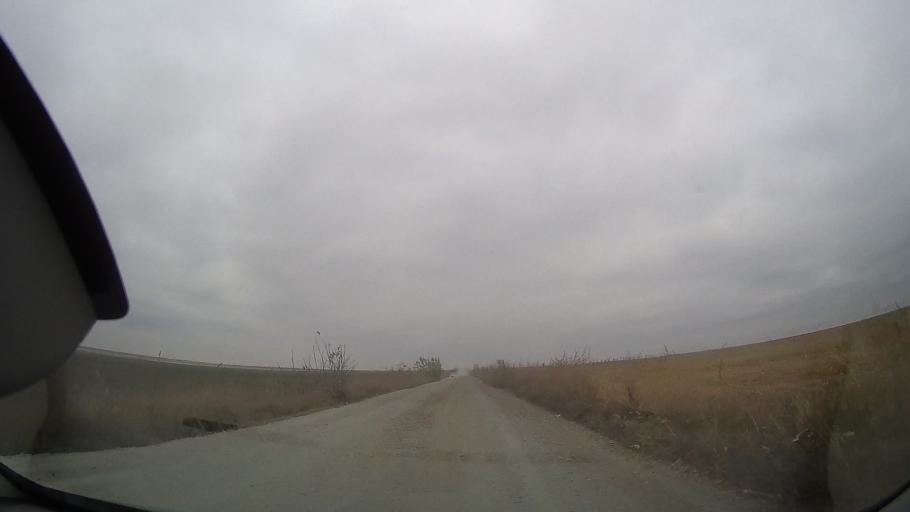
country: RO
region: Ialomita
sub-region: Comuna Grivita
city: Grivita
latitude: 44.7467
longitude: 27.2680
